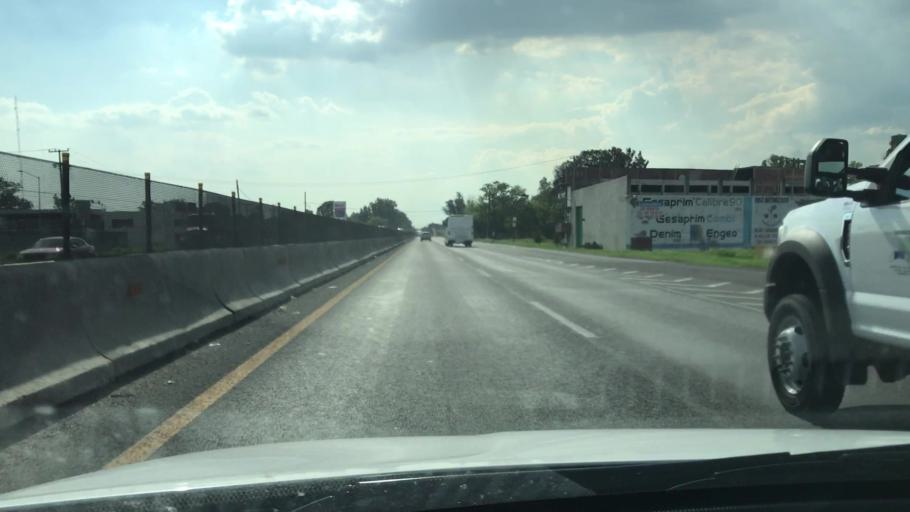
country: MX
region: Guanajuato
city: Valtierrilla
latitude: 20.5496
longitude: -101.1411
